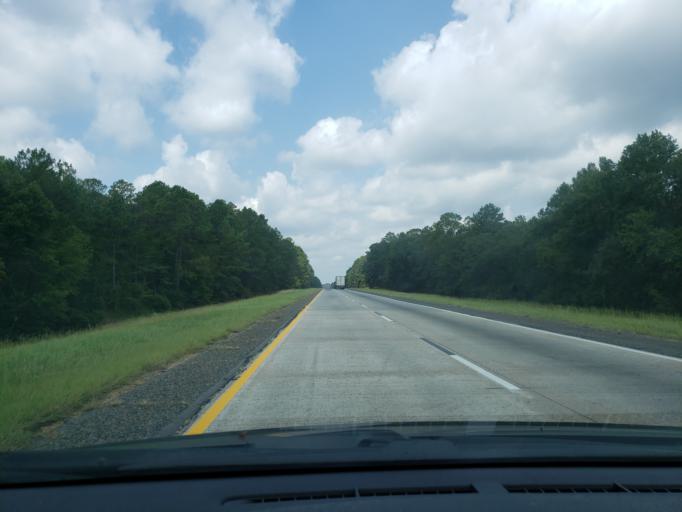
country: US
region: Georgia
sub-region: Treutlen County
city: Soperton
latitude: 32.4270
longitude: -82.5522
